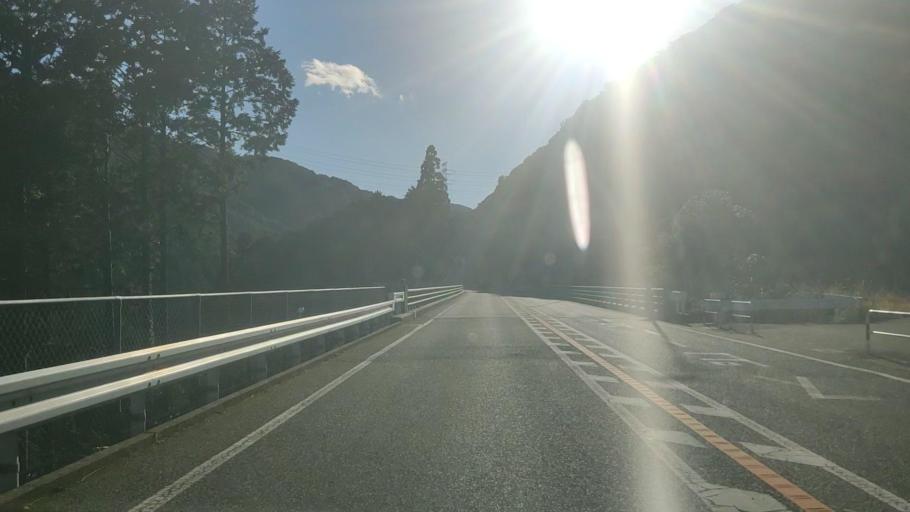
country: JP
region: Fukuoka
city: Maebaru-chuo
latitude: 33.4889
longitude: 130.2920
